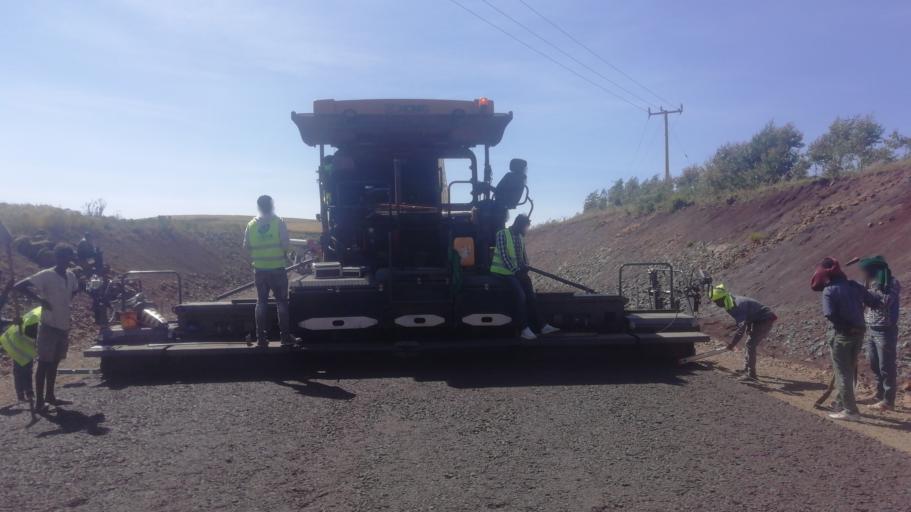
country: ET
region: Amhara
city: Addiet Canna
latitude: 11.3650
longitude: 37.8710
